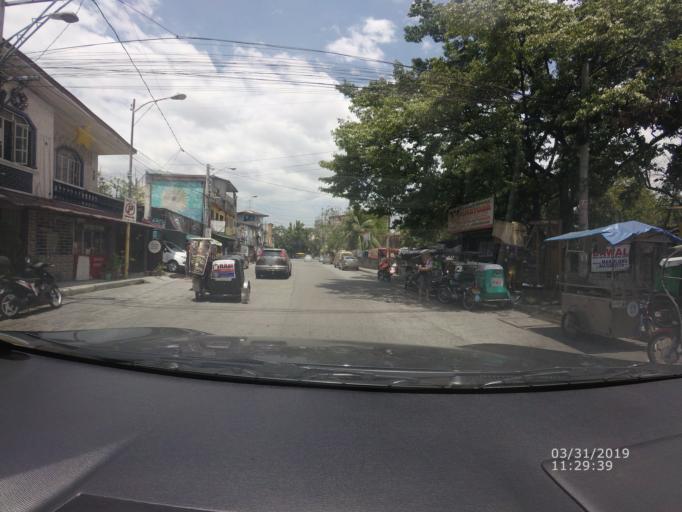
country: PH
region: Metro Manila
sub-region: Mandaluyong
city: Mandaluyong City
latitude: 14.5812
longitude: 121.0450
